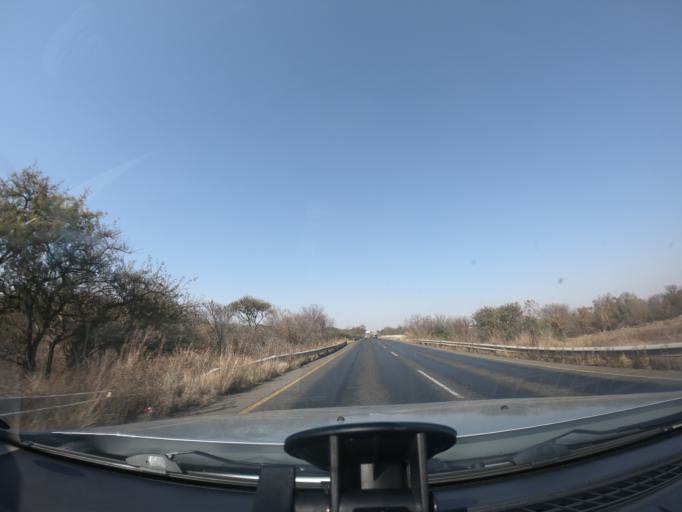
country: ZA
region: KwaZulu-Natal
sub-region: uThukela District Municipality
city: Ladysmith
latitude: -28.7408
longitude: 29.8186
